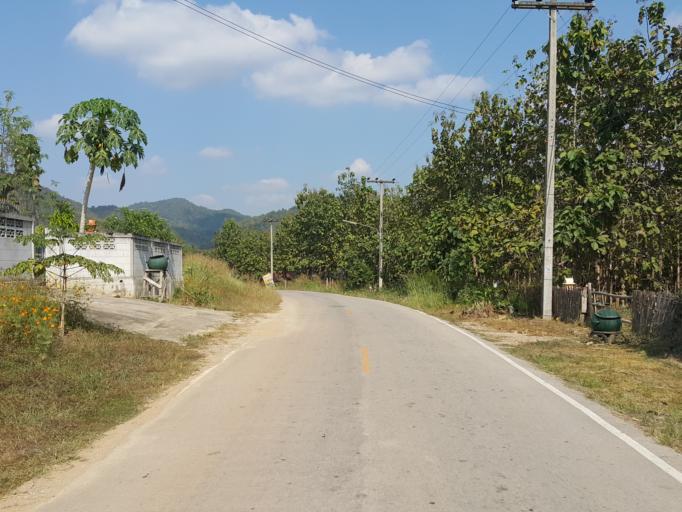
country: TH
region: Sukhothai
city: Thung Saliam
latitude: 17.3403
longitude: 99.4607
